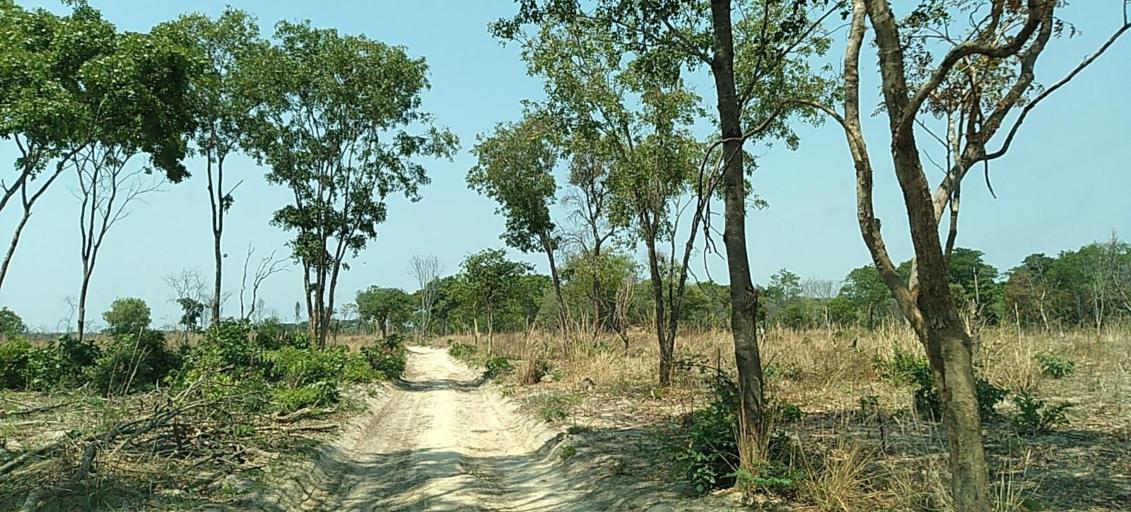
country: ZM
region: Copperbelt
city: Mpongwe
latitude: -13.8703
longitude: 28.0492
